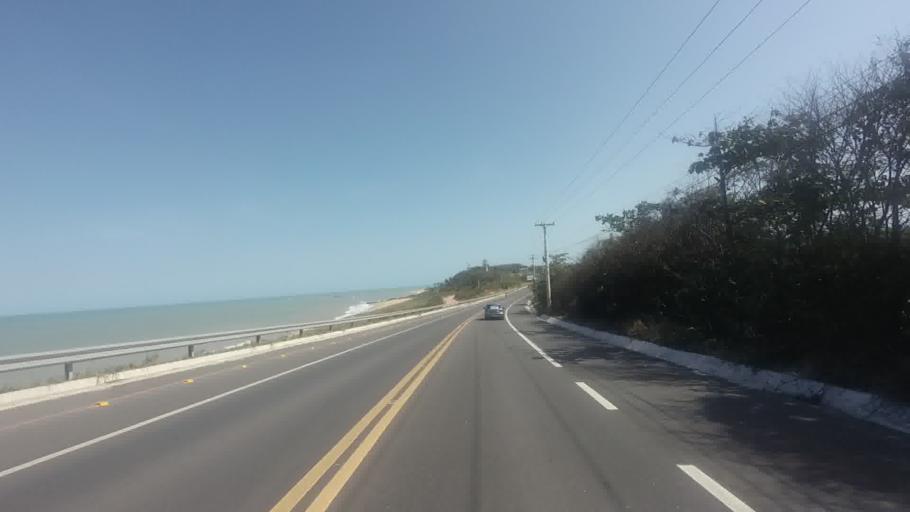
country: BR
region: Espirito Santo
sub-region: Piuma
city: Piuma
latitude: -20.8144
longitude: -40.6137
